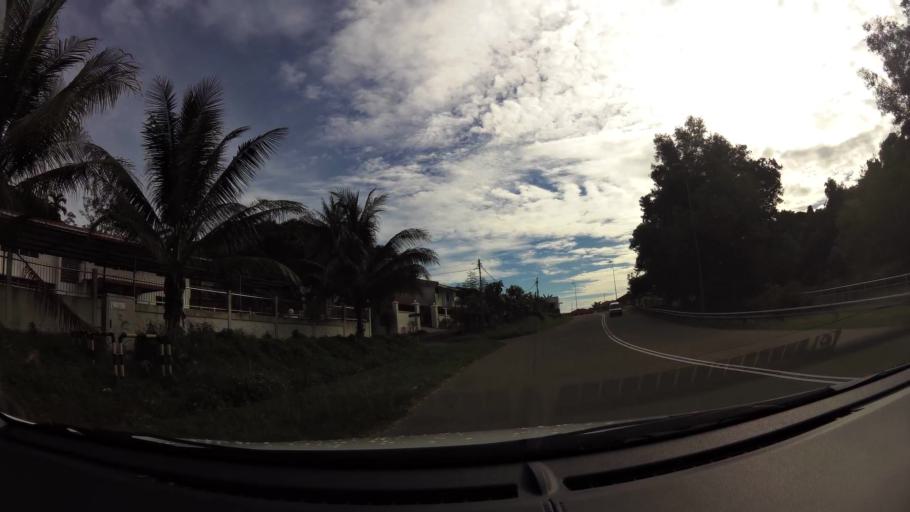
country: BN
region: Brunei and Muara
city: Bandar Seri Begawan
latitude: 4.8876
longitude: 114.9603
